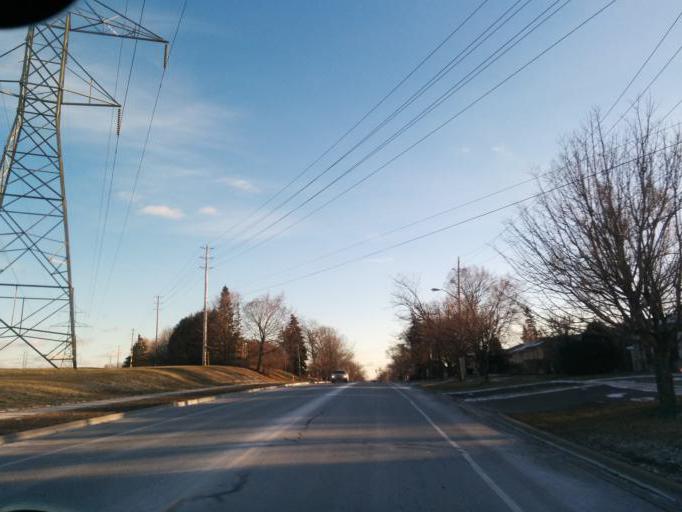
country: CA
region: Ontario
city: Etobicoke
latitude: 43.6711
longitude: -79.5616
